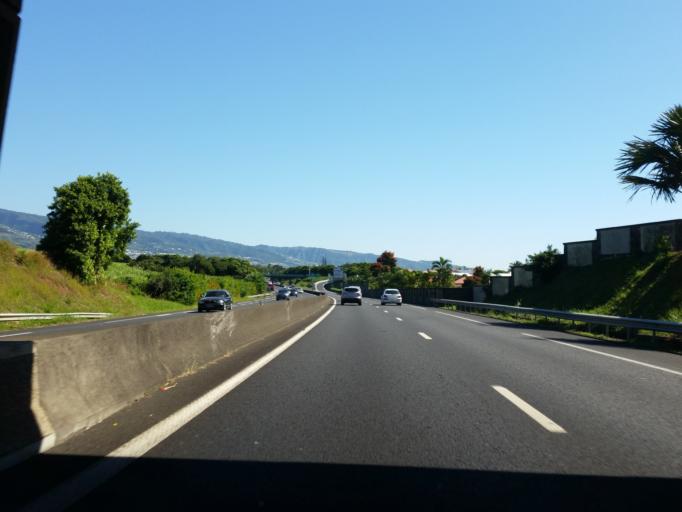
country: RE
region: Reunion
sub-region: Reunion
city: Sainte-Marie
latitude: -20.9024
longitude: 55.5480
